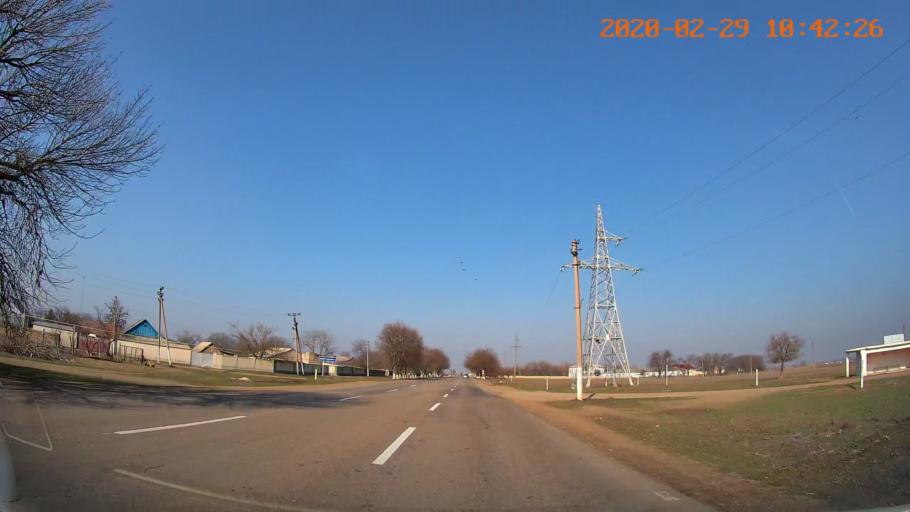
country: MD
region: Telenesti
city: Grigoriopol
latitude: 47.0516
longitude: 29.4110
